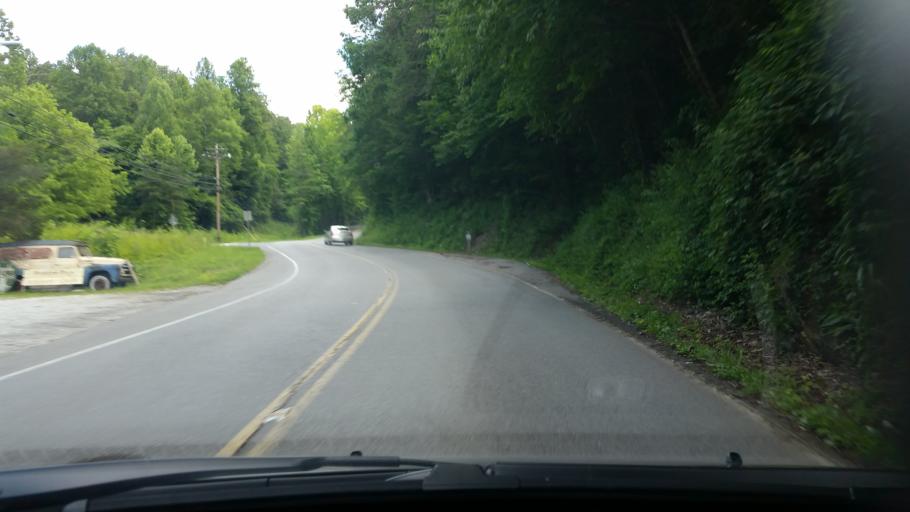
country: US
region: Tennessee
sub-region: Sevier County
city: Gatlinburg
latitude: 35.7363
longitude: -83.4674
